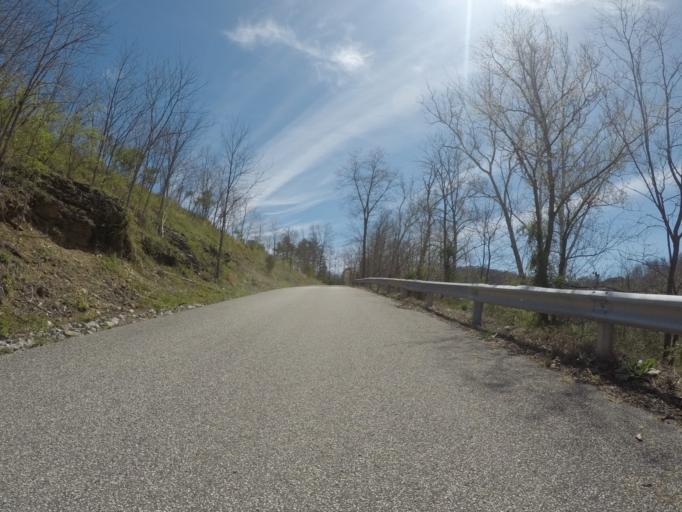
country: US
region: West Virginia
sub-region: Cabell County
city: Barboursville
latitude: 38.4083
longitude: -82.3061
